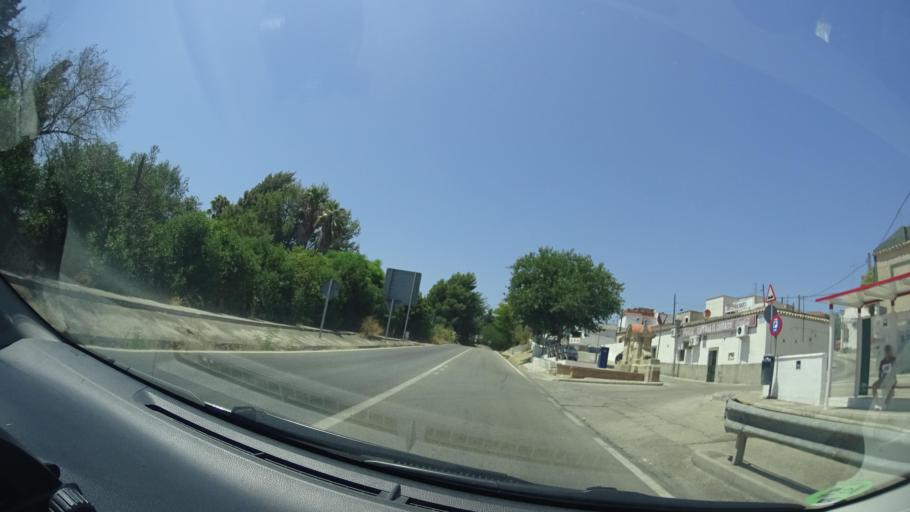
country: ES
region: Andalusia
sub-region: Provincia de Cadiz
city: Jerez de la Frontera
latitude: 36.6589
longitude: -6.1011
